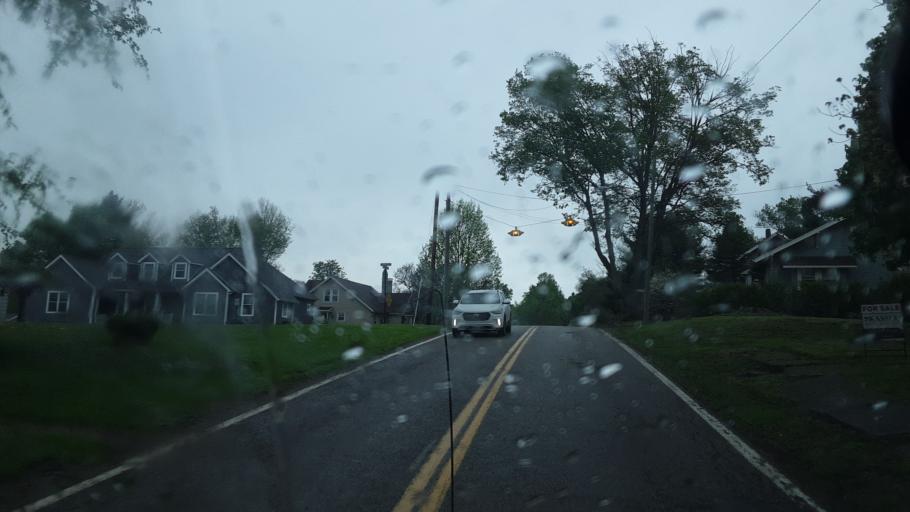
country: US
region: Ohio
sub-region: Muskingum County
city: New Concord
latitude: 39.9965
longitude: -81.7427
